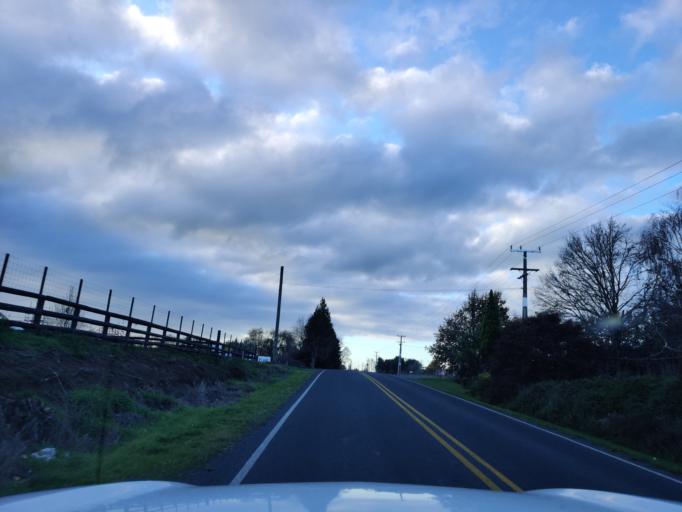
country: NZ
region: Waikato
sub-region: Waipa District
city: Cambridge
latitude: -37.8524
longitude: 175.4390
